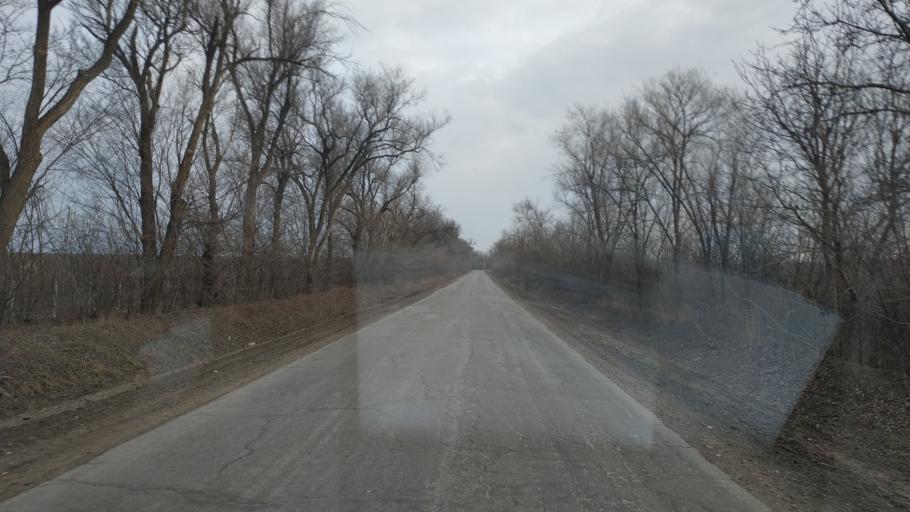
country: MD
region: Chisinau
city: Singera
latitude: 46.9386
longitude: 29.0480
